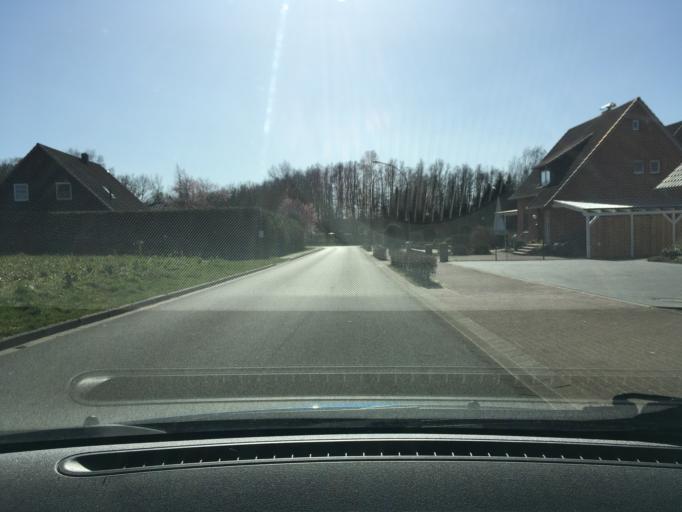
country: DE
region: Lower Saxony
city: Ebstorf
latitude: 53.0202
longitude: 10.4055
